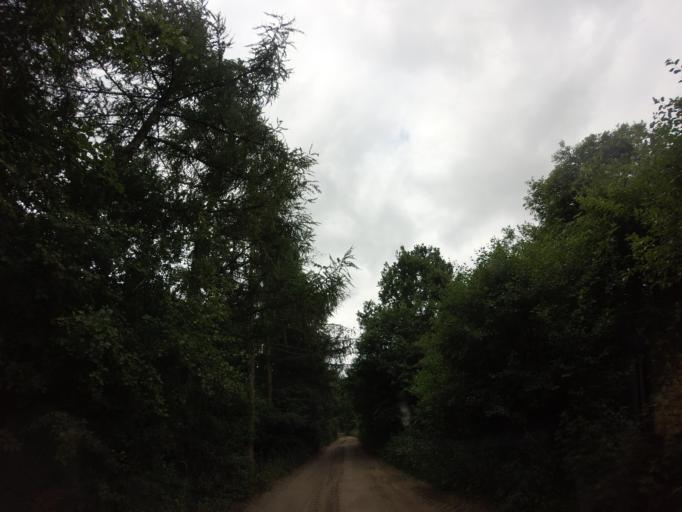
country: PL
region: Lubusz
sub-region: Powiat strzelecko-drezdenecki
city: Strzelce Krajenskie
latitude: 52.9428
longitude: 15.6074
